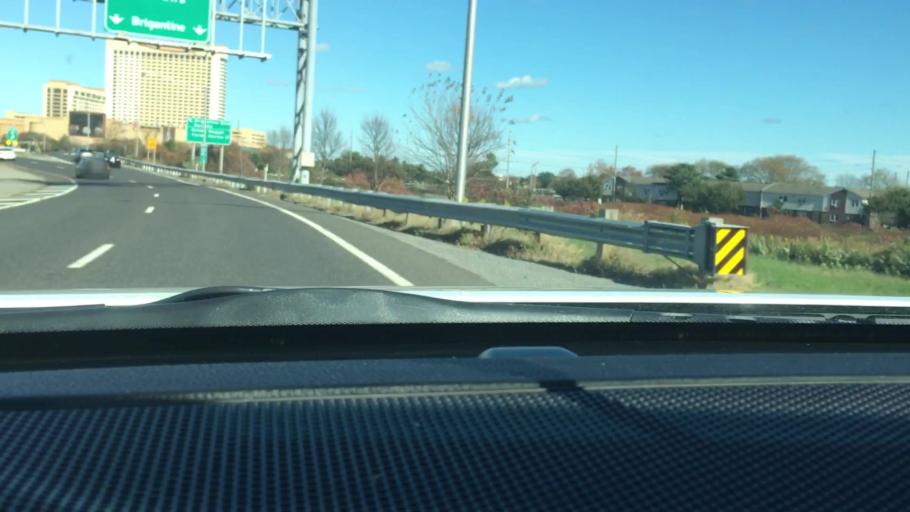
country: US
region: New Jersey
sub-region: Atlantic County
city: Atlantic City
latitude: 39.3749
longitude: -74.4333
